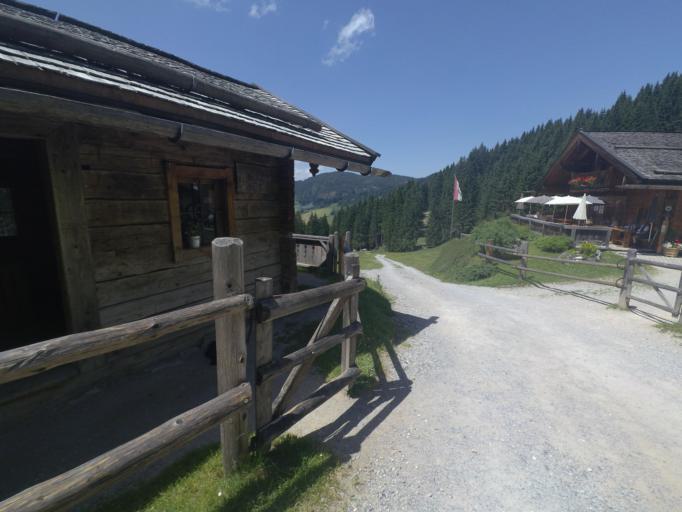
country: AT
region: Salzburg
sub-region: Politischer Bezirk Zell am See
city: Dienten am Hochkonig
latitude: 47.4116
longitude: 12.9947
